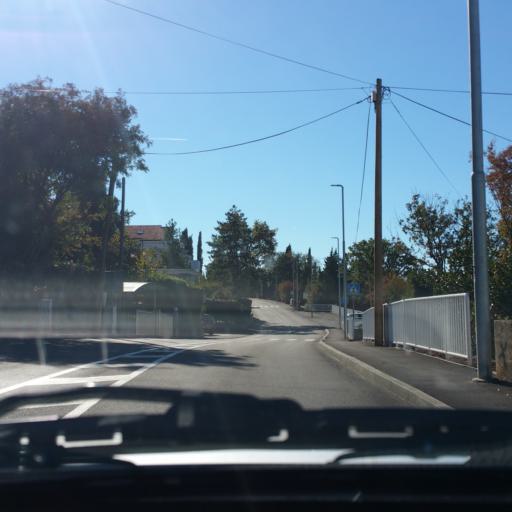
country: HR
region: Primorsko-Goranska
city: Njivice
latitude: 45.1609
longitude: 14.5395
